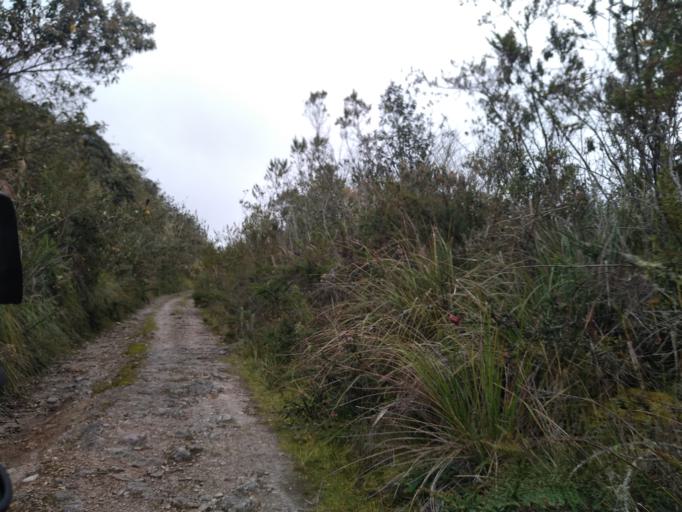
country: EC
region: Carchi
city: San Gabriel
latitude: 0.7020
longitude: -77.8416
